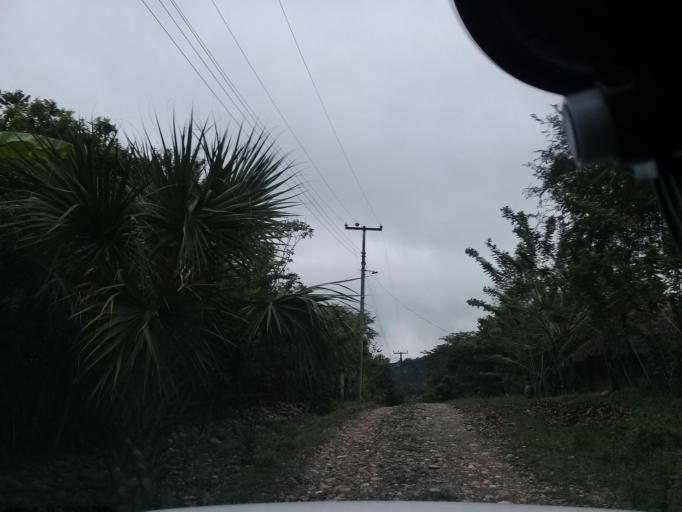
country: MX
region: Veracruz
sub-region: Chalma
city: San Pedro Coyutla
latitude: 21.2218
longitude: -98.4286
